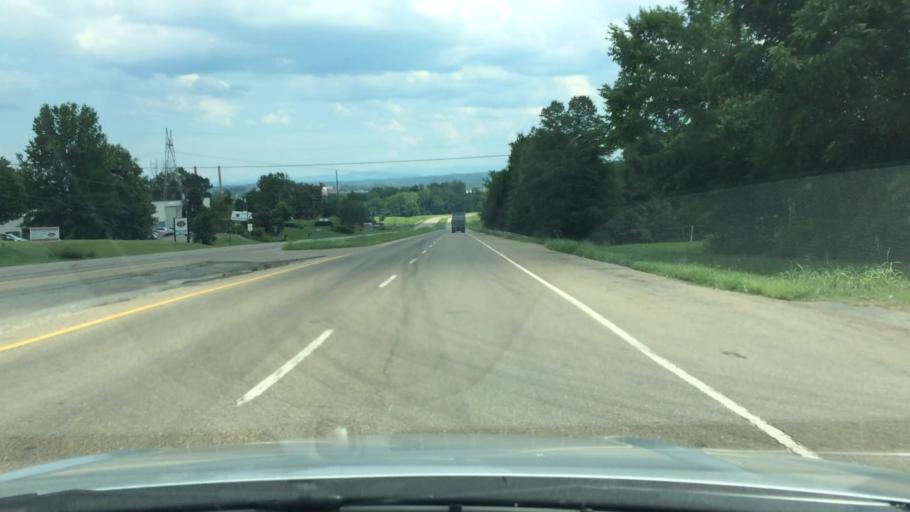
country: US
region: Tennessee
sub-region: Jefferson County
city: White Pine
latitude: 36.1659
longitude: -83.2175
